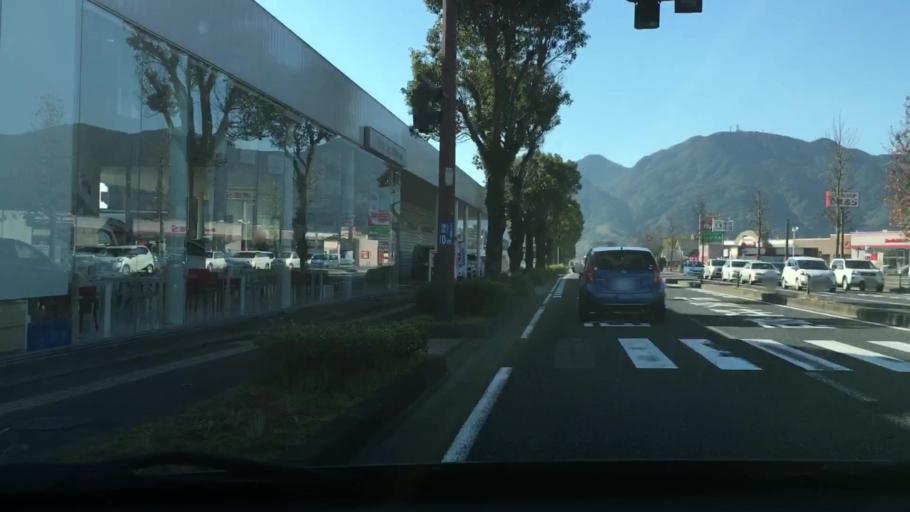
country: JP
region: Kagoshima
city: Kajiki
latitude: 31.7223
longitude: 130.6222
